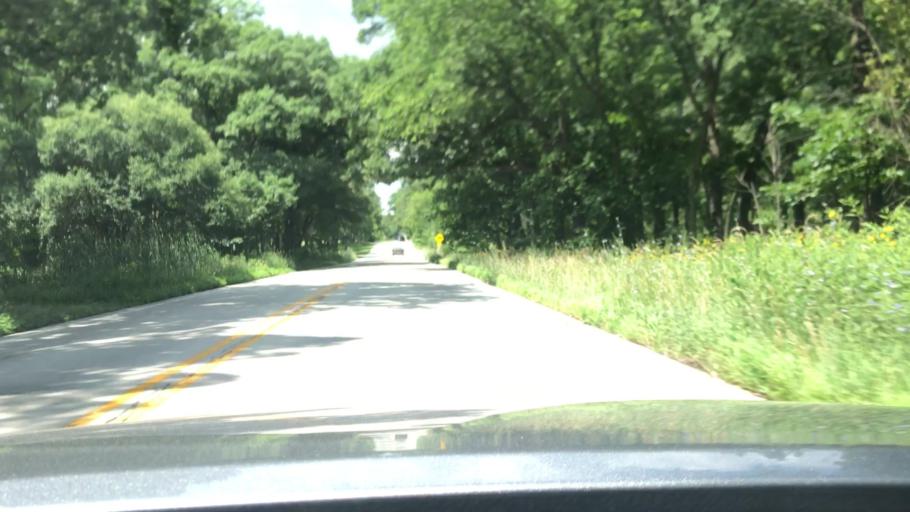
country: US
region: Illinois
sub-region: Cook County
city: Willow Springs
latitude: 41.7176
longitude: -87.8646
